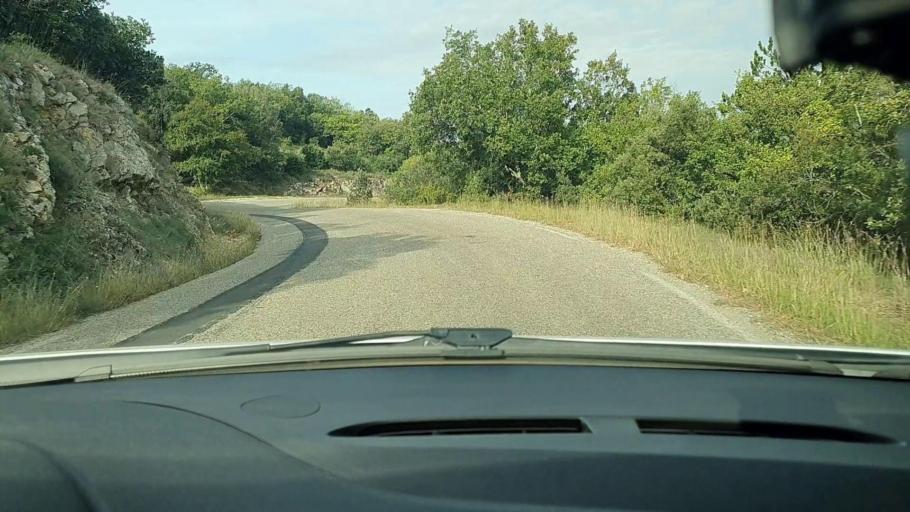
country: FR
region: Languedoc-Roussillon
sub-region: Departement du Gard
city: Saint-Quentin-la-Poterie
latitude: 44.1270
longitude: 4.4073
